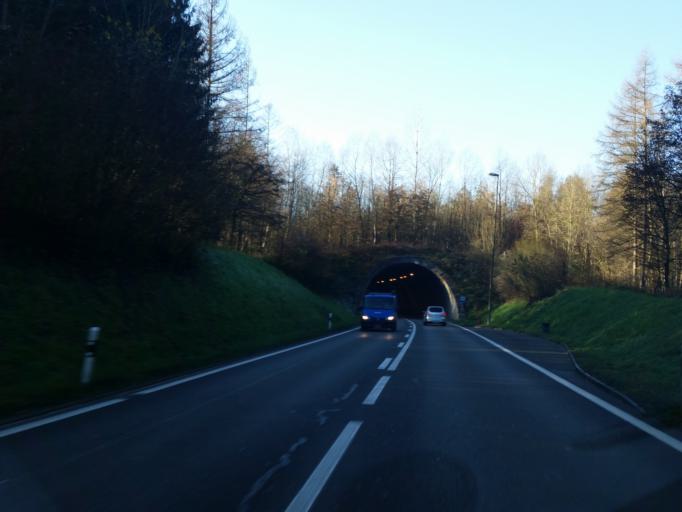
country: CH
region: Aargau
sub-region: Bezirk Bremgarten
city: Bremgarten
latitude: 47.3606
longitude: 8.3407
